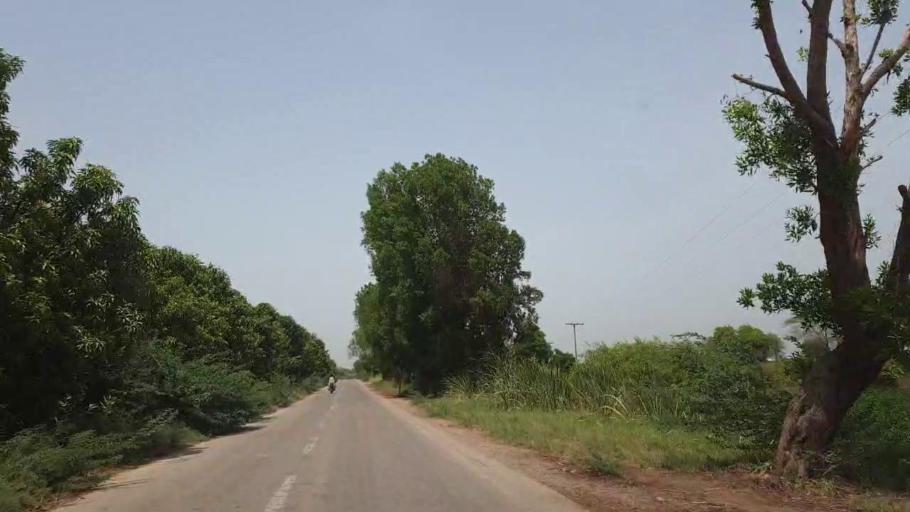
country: PK
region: Sindh
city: Sakrand
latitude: 26.1914
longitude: 68.2357
